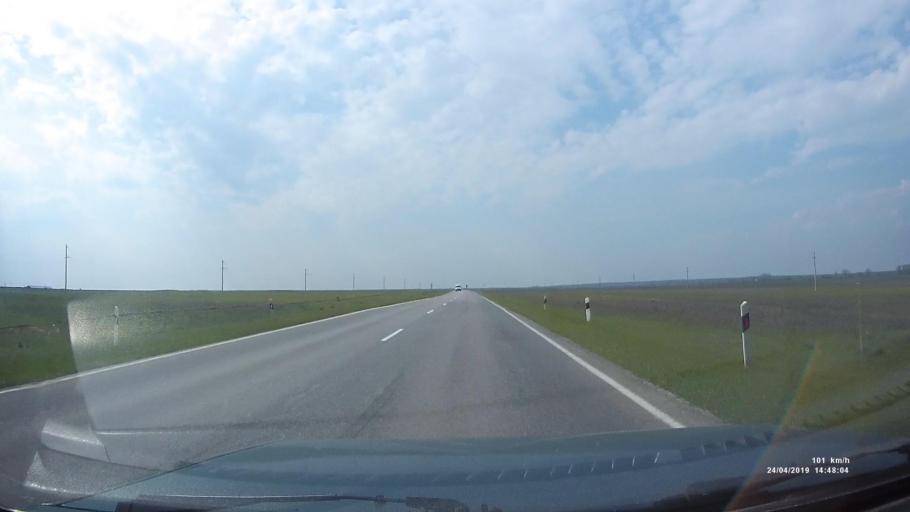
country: RU
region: Rostov
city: Remontnoye
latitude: 46.4970
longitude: 43.7629
